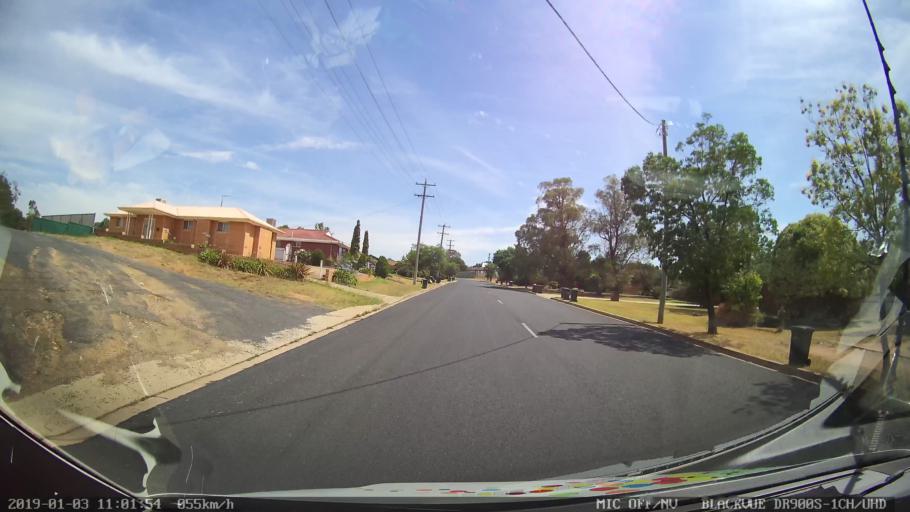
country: AU
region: New South Wales
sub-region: Young
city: Young
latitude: -34.3018
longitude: 148.2992
